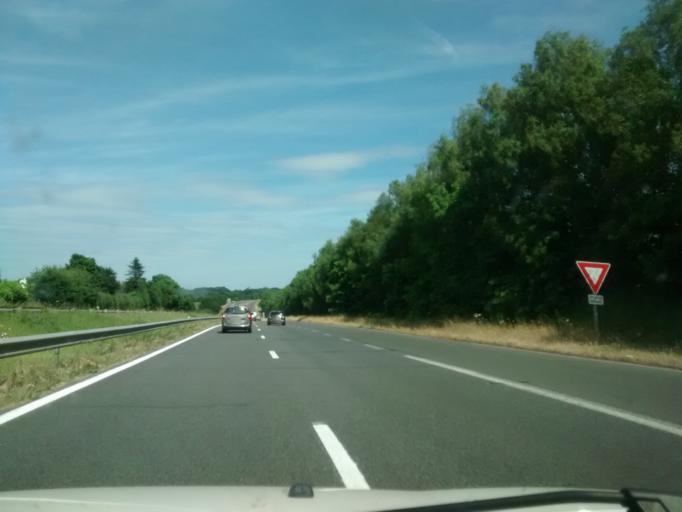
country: FR
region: Brittany
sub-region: Departement des Cotes-d'Armor
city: Plelo
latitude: 48.5314
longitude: -2.9325
